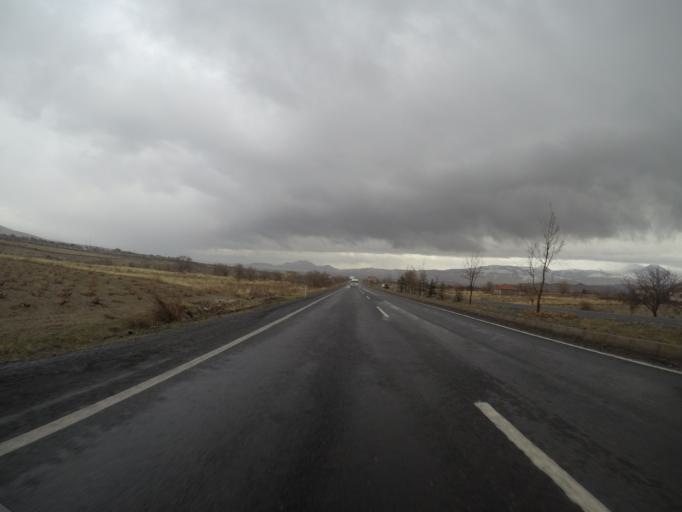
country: TR
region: Kayseri
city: Incesu
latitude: 38.6811
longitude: 35.2117
